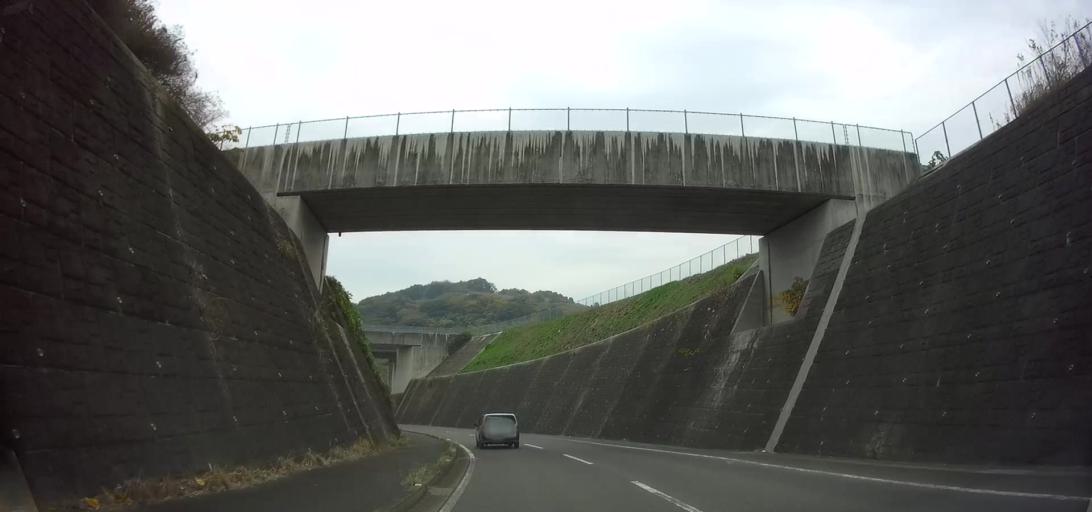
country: JP
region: Nagasaki
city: Shimabara
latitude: 32.7051
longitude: 130.1904
